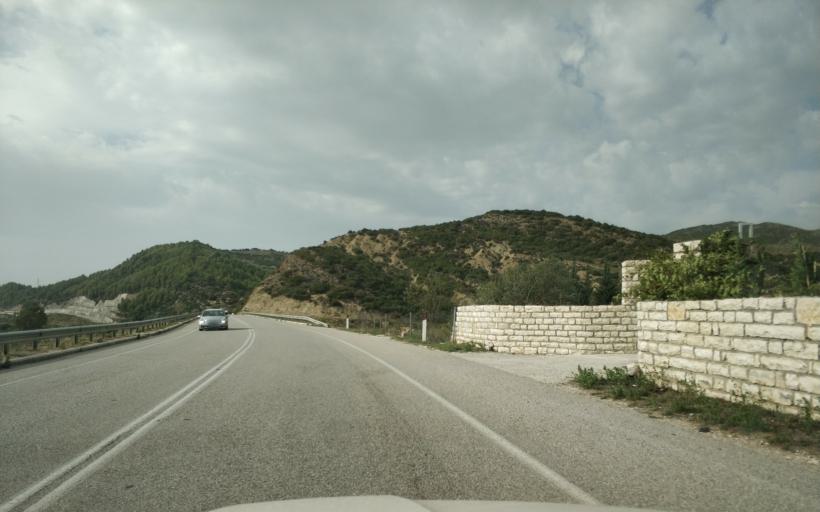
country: AL
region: Gjirokaster
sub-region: Rrethi i Tepelenes
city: Memaliaj
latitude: 40.3786
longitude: 19.9052
